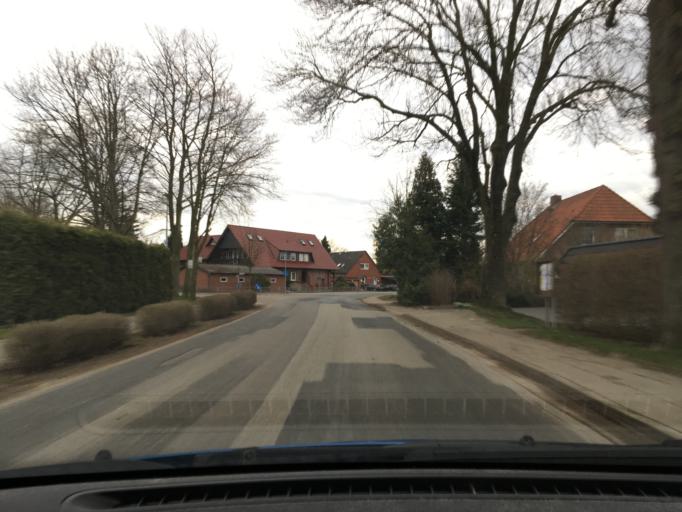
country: DE
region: Lower Saxony
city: Handorf
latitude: 53.3639
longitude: 10.3366
